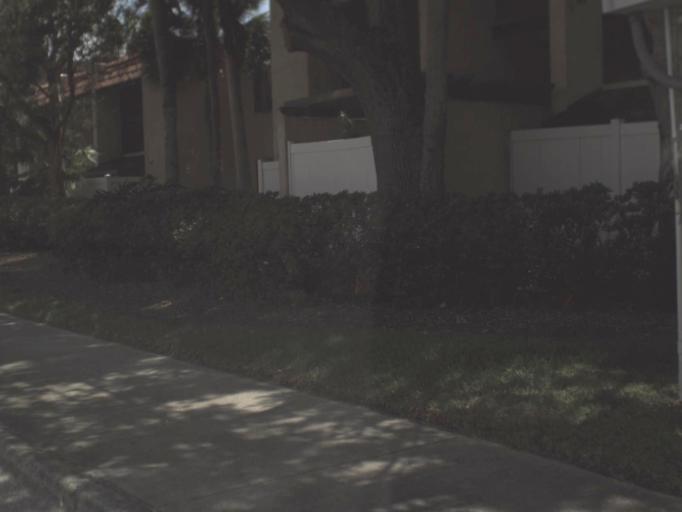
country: US
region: Florida
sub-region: Hillsborough County
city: Tampa
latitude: 27.9448
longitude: -82.5330
